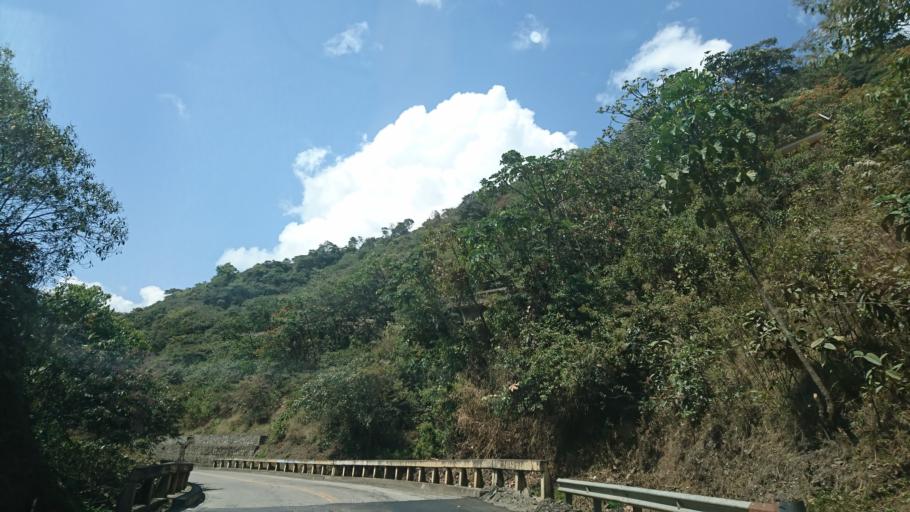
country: BO
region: La Paz
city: Coroico
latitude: -16.2075
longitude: -67.8038
